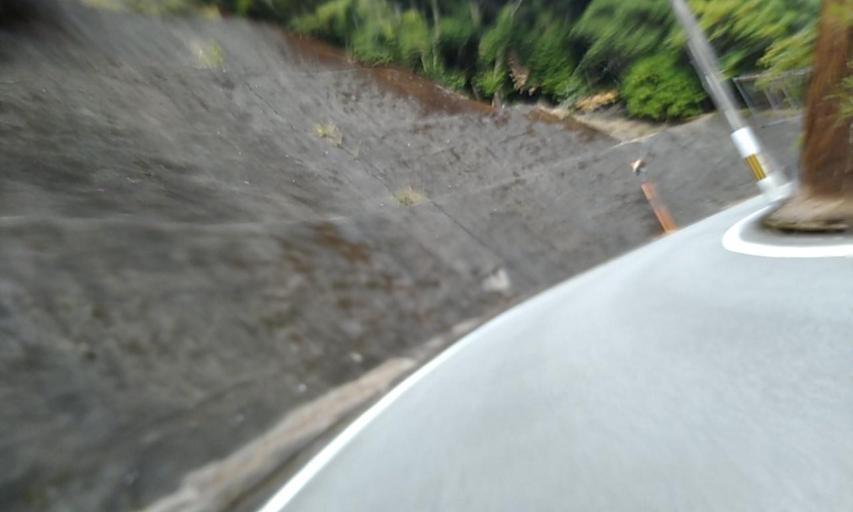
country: JP
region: Wakayama
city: Shingu
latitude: 33.5456
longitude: 135.8466
